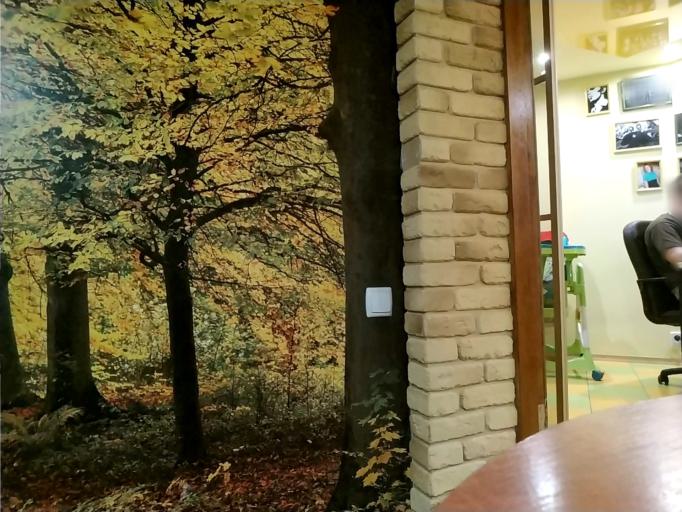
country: RU
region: Tverskaya
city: Zapadnaya Dvina
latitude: 56.3261
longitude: 31.9056
